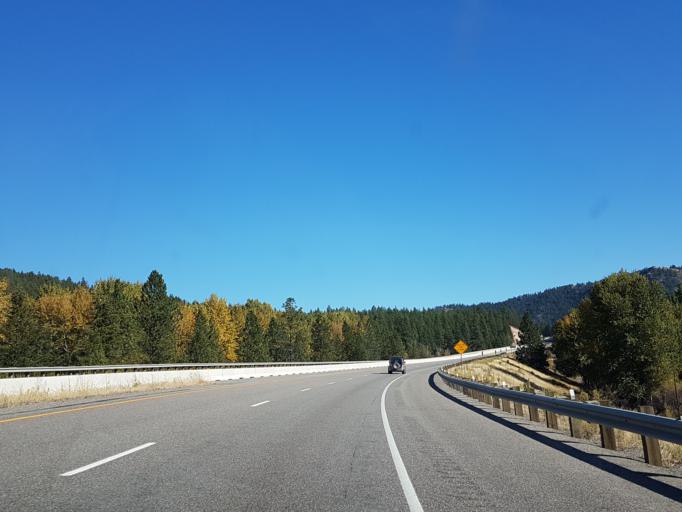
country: US
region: Montana
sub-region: Missoula County
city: Frenchtown
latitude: 47.0232
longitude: -114.3881
